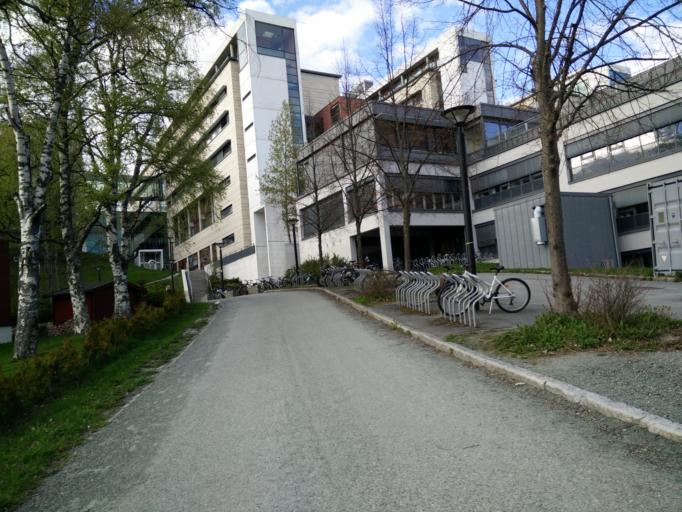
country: NO
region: Sor-Trondelag
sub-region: Trondheim
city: Trondheim
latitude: 63.4147
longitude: 10.4058
